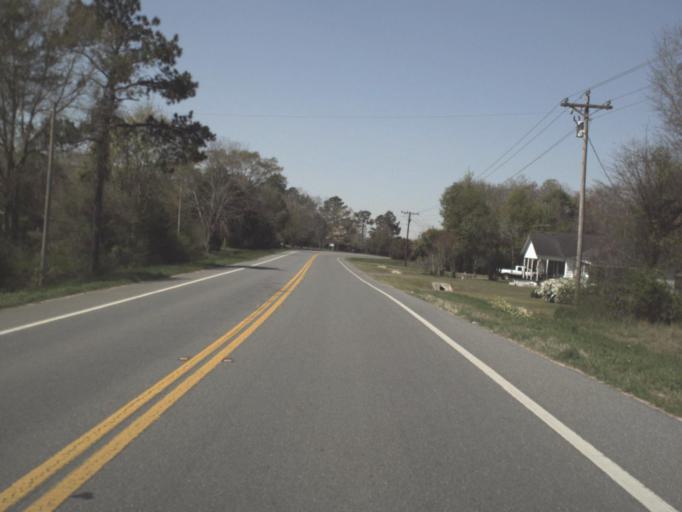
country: US
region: Florida
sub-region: Jackson County
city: Graceville
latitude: 30.9637
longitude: -85.5651
